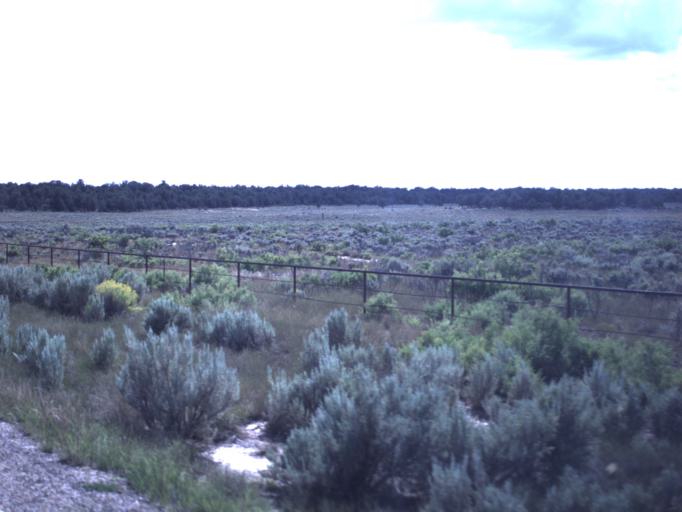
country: US
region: Utah
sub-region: Duchesne County
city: Duchesne
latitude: 40.2686
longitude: -110.7046
